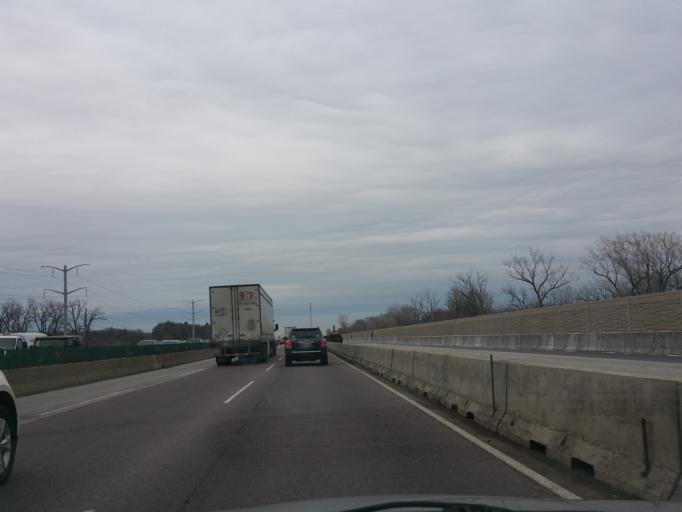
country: US
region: Illinois
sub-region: Cook County
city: South Barrington
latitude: 42.0664
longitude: -88.1186
